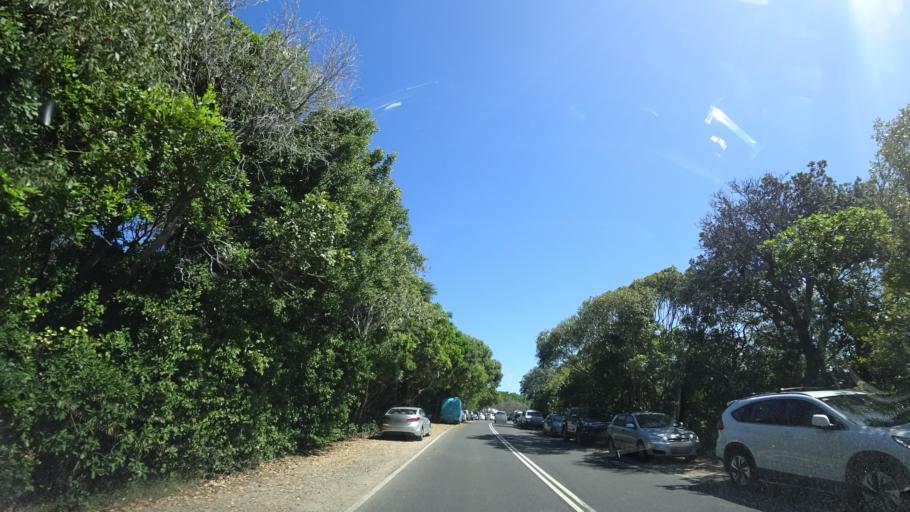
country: AU
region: Queensland
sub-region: Sunshine Coast
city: Mooloolaba
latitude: -26.6374
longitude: 153.1016
